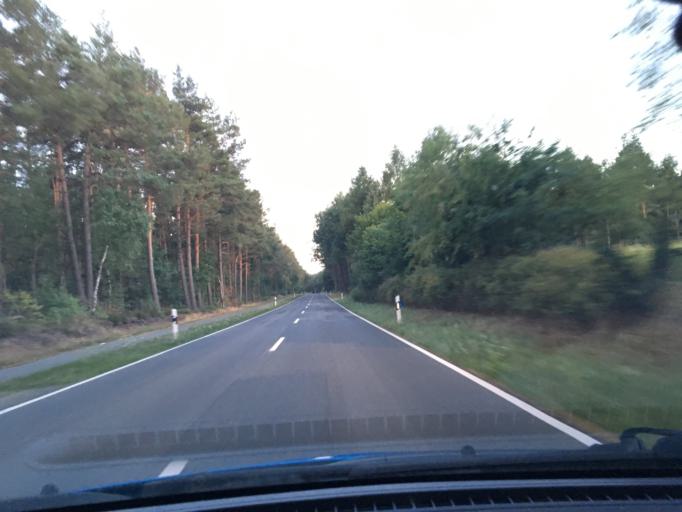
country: DE
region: Lower Saxony
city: Fassberg
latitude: 52.9082
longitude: 10.1525
